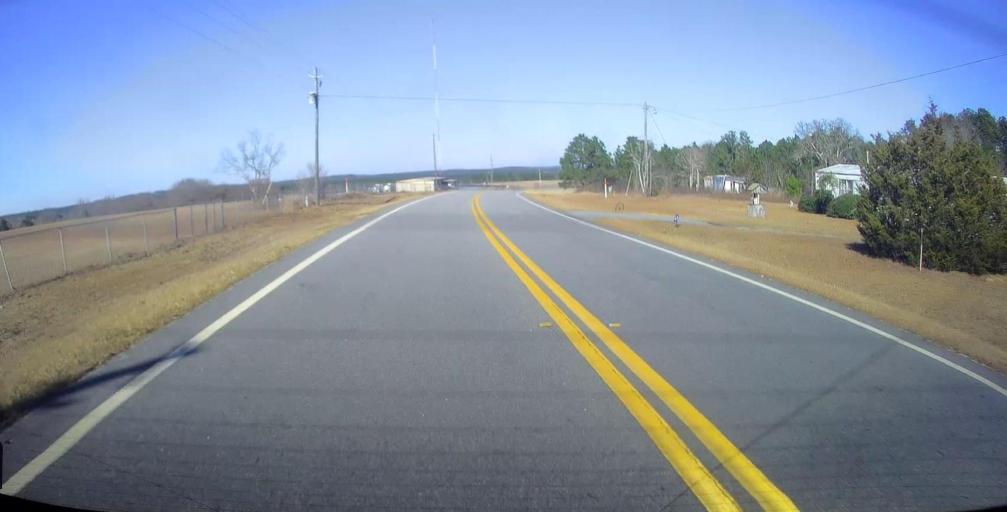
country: US
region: Georgia
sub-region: Taylor County
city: Butler
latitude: 32.5678
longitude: -84.2233
